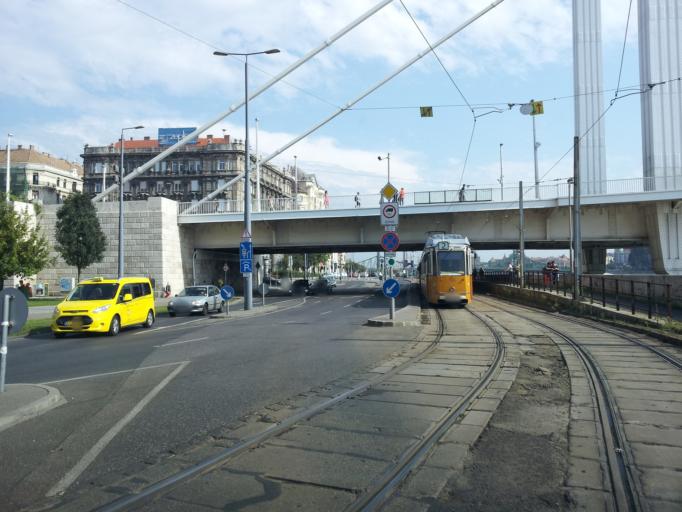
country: HU
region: Budapest
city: Budapest I. keruelet
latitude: 47.4921
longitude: 19.0507
